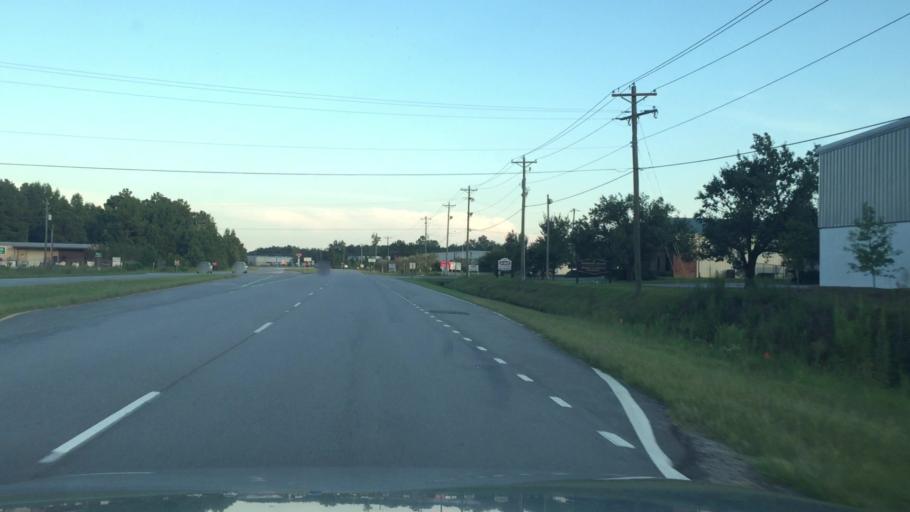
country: US
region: South Carolina
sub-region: Richland County
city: Forest Acres
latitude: 33.9453
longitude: -80.9626
